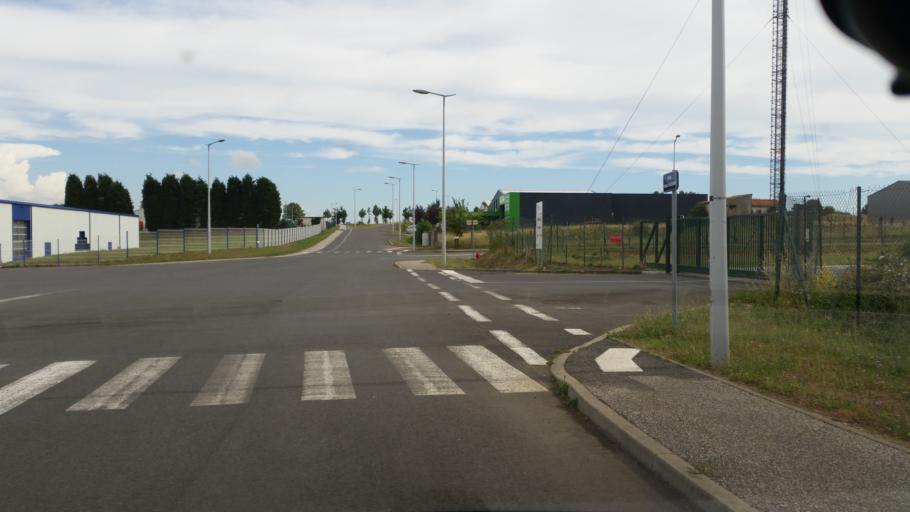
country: FR
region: Poitou-Charentes
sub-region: Departement de la Charente-Maritime
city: Surgeres
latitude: 46.1102
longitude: -0.7795
